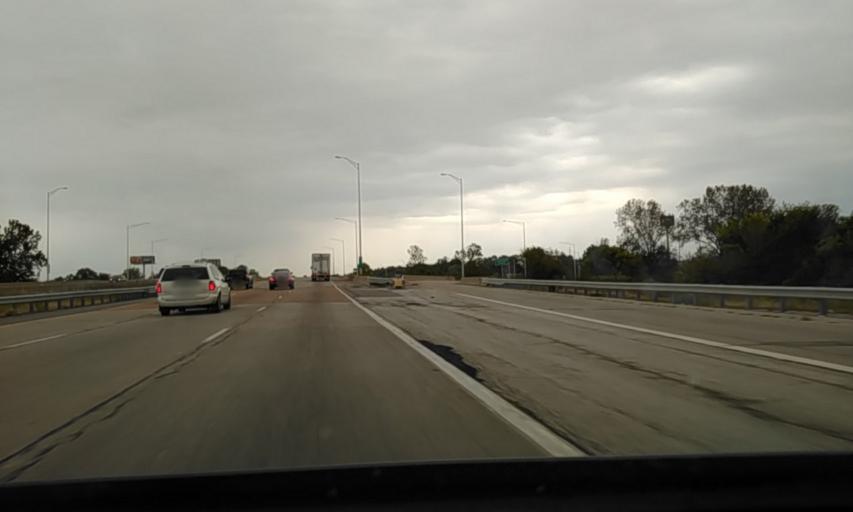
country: US
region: Illinois
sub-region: Saint Clair County
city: Caseyville
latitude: 38.6562
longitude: -90.0320
